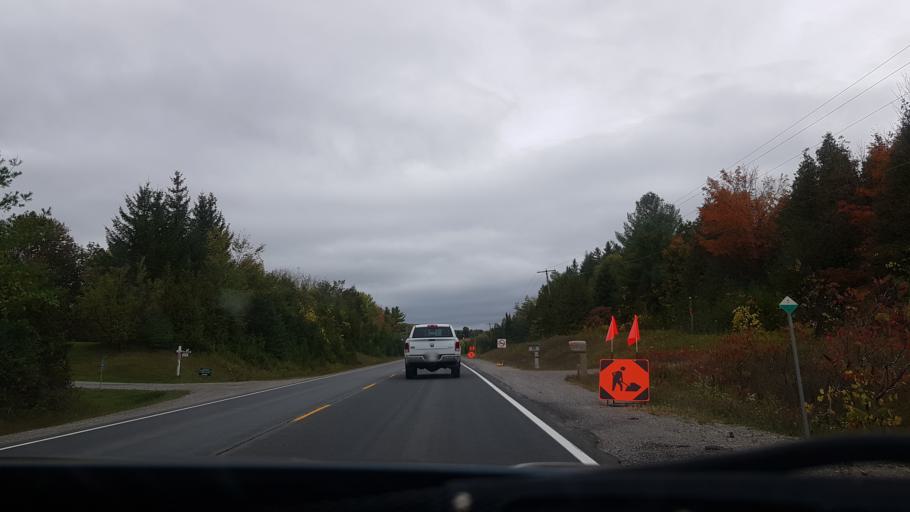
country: CA
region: Ontario
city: Omemee
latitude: 44.1932
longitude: -78.4954
